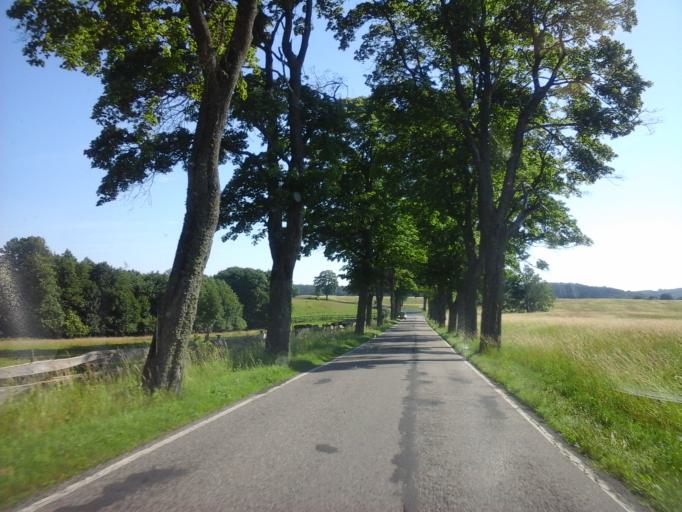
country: PL
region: West Pomeranian Voivodeship
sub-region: Powiat drawski
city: Zlocieniec
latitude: 53.6076
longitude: 15.9174
